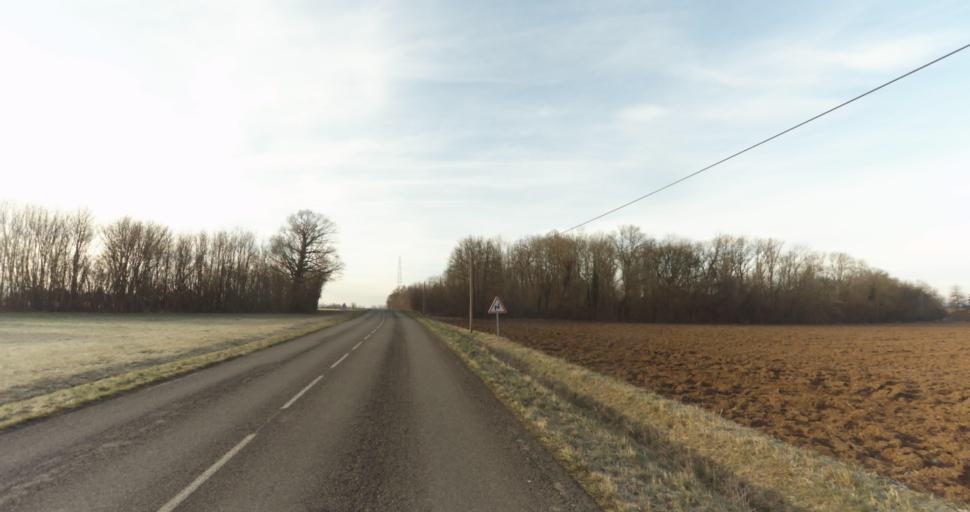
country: FR
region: Lorraine
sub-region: Departement de Meurthe-et-Moselle
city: Giraumont
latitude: 49.1729
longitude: 5.8972
